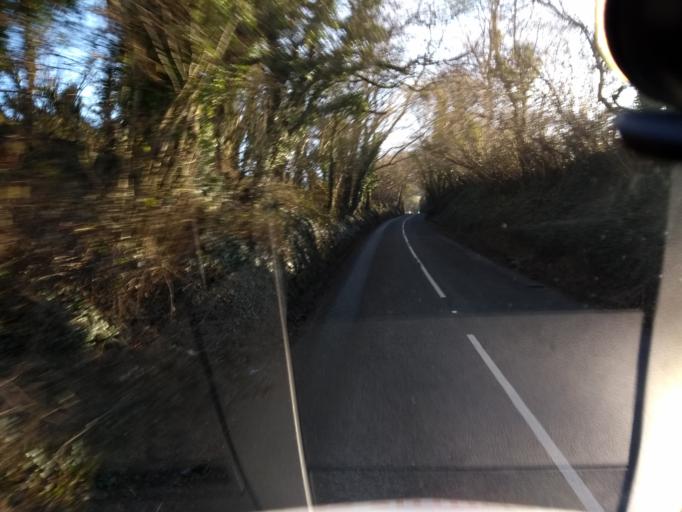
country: GB
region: England
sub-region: Somerset
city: Bruton
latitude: 51.1068
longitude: -2.4401
